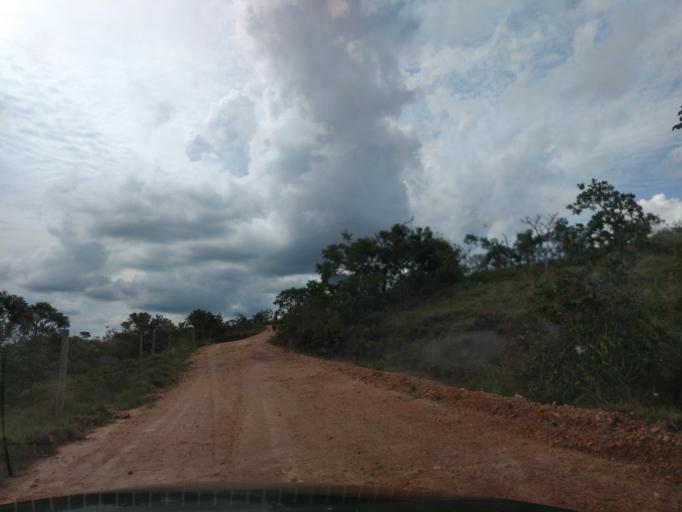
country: BR
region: Minas Gerais
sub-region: Lavras
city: Lavras
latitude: -21.5298
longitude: -44.8898
